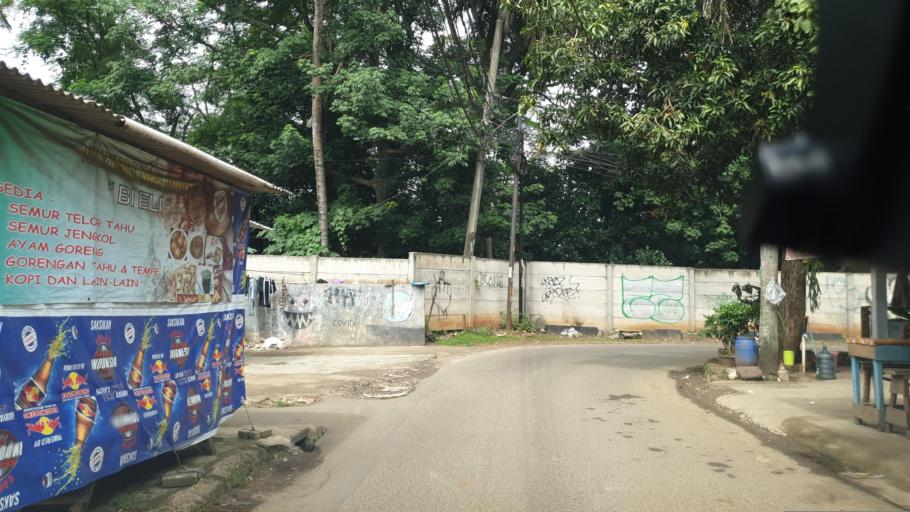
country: ID
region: West Java
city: Pamulang
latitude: -6.3473
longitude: 106.7688
